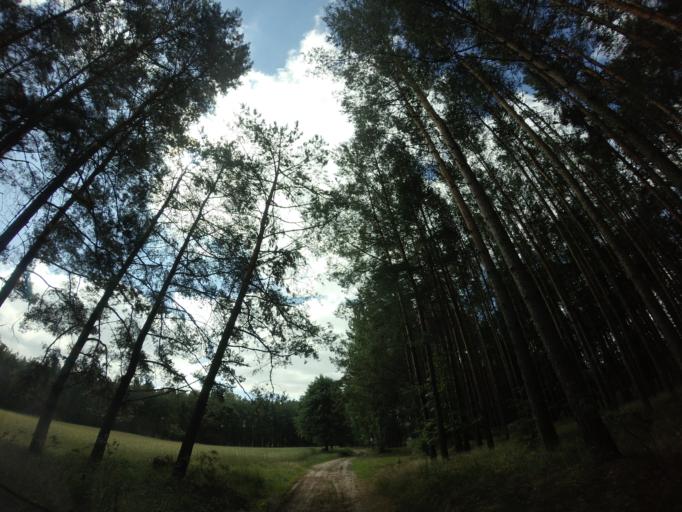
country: PL
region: Lubusz
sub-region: Powiat strzelecko-drezdenecki
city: Dobiegniew
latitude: 53.0066
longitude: 15.7129
